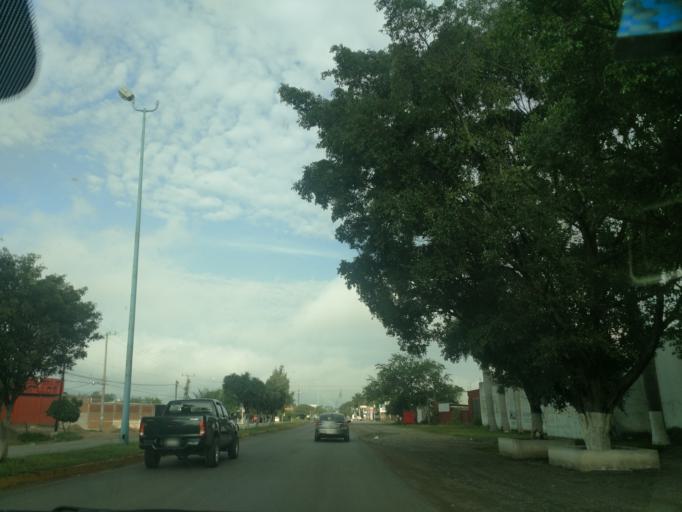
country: MX
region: Jalisco
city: Ameca
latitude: 20.5360
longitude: -104.0305
